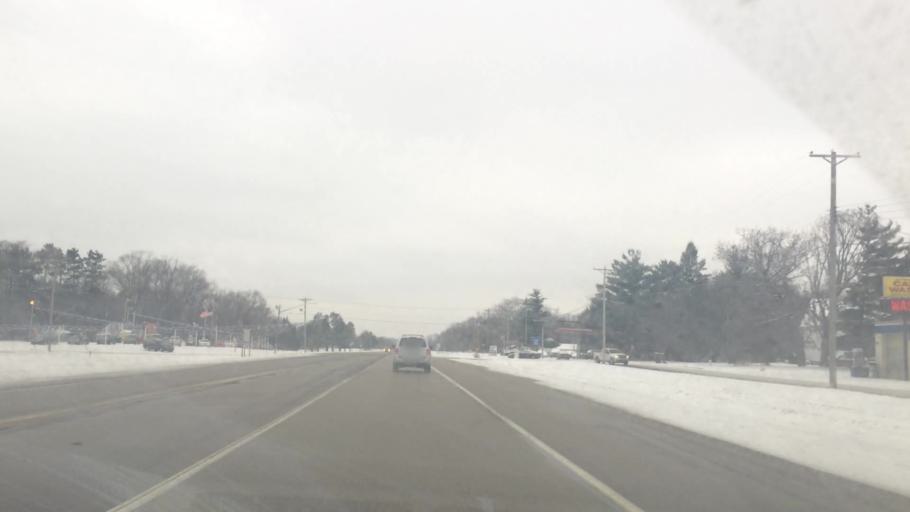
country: US
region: Minnesota
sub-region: Anoka County
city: Lexington
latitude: 45.1364
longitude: -93.1720
